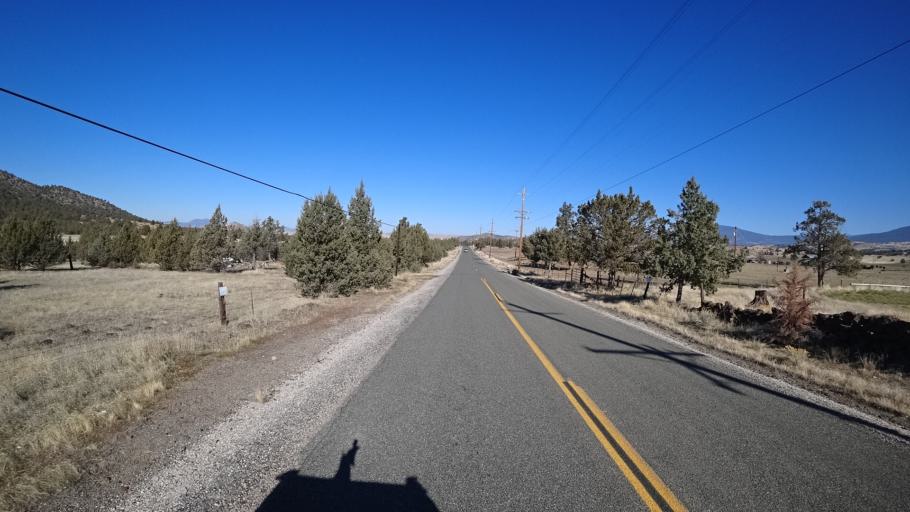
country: US
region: California
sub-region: Siskiyou County
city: Montague
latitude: 41.6670
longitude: -122.3695
